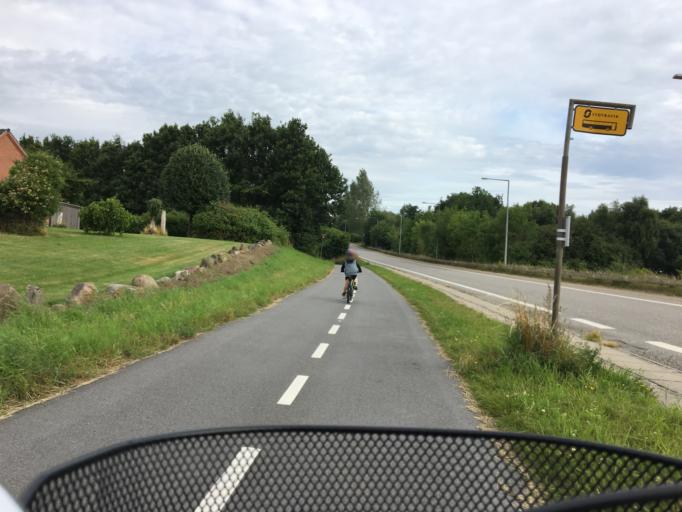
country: DK
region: South Denmark
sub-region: Fredericia Kommune
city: Snoghoj
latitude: 55.5277
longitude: 9.7322
